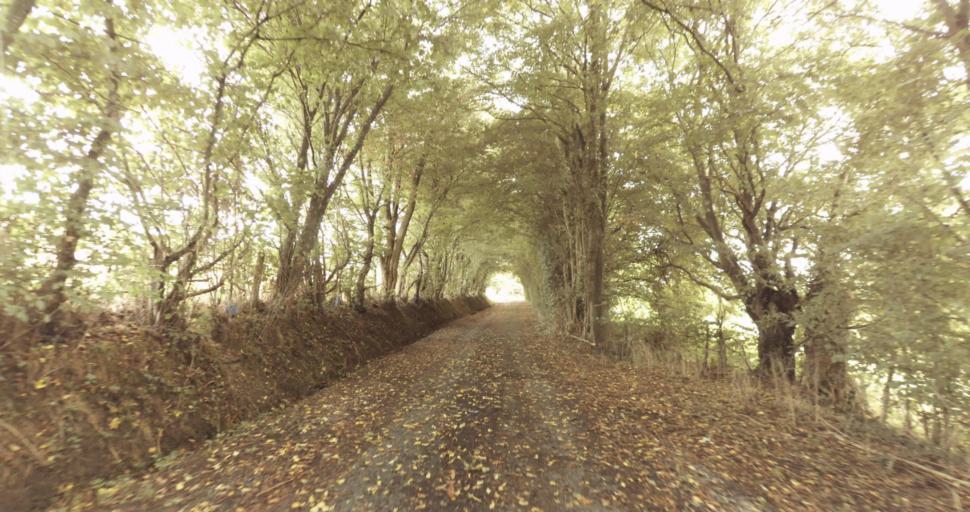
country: FR
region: Lower Normandy
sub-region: Departement de l'Orne
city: Sainte-Gauburge-Sainte-Colombe
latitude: 48.7072
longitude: 0.3924
